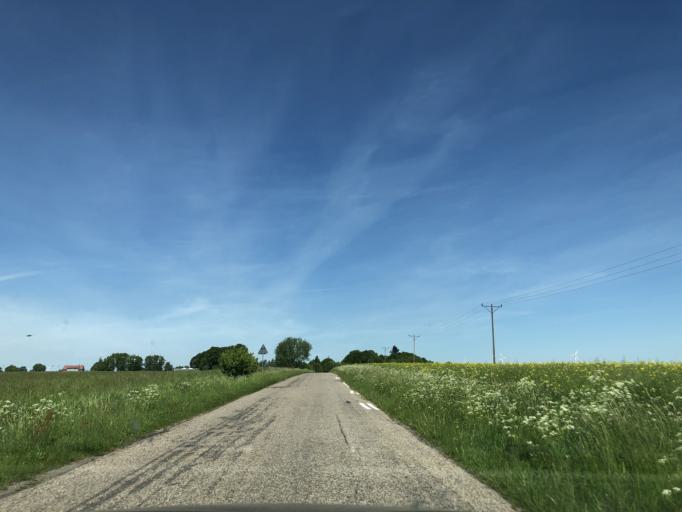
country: PL
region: West Pomeranian Voivodeship
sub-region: Powiat kolobrzeski
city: Goscino
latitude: 54.0034
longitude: 15.7188
